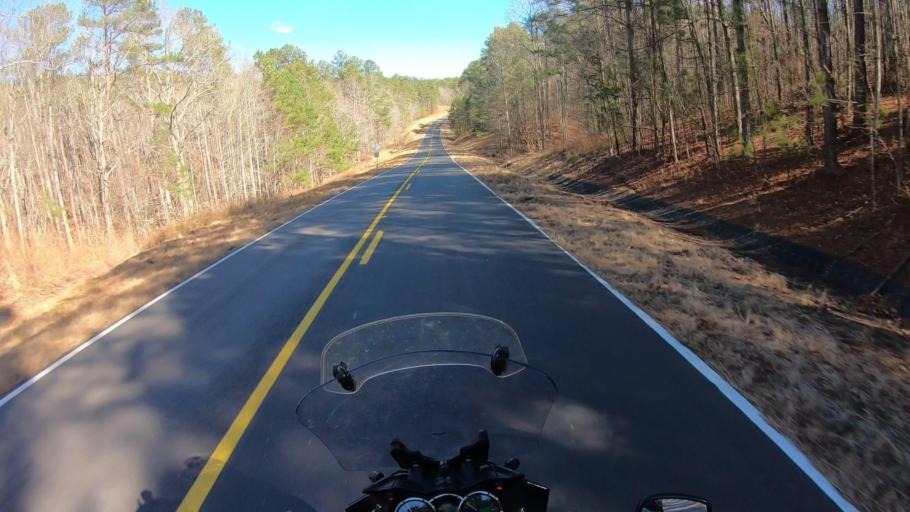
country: US
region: Alabama
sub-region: Talladega County
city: Munford
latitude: 33.4209
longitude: -85.8710
